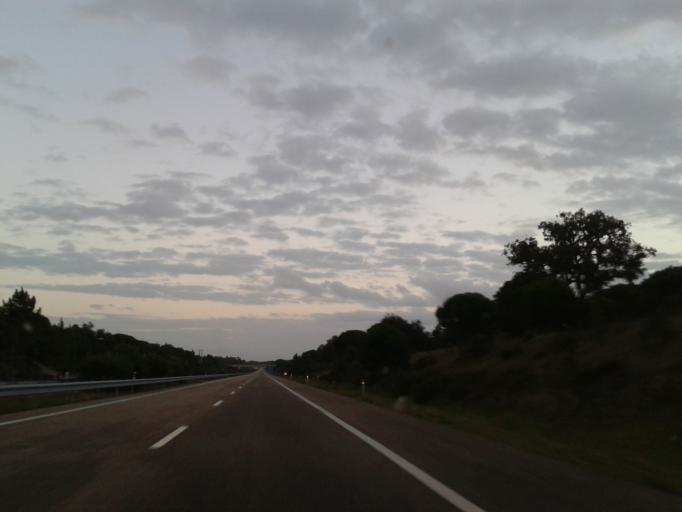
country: PT
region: Evora
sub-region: Vendas Novas
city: Vendas Novas
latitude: 38.6273
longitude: -8.6585
